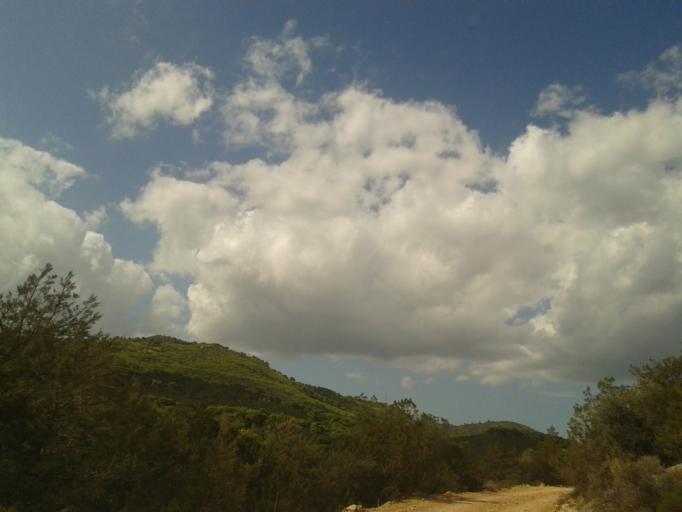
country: GR
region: Attica
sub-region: Nomarchia Anatolikis Attikis
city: Kato Soulion
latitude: 38.2165
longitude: 24.0190
